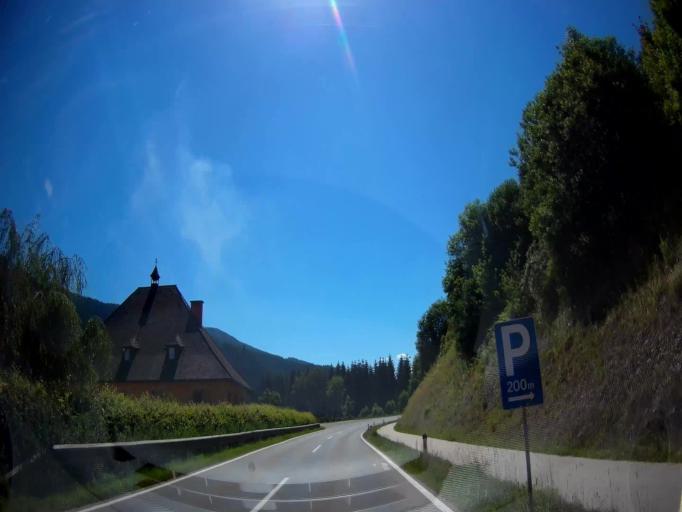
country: AT
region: Carinthia
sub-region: Politischer Bezirk Sankt Veit an der Glan
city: Gurk
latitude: 46.8682
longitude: 14.2684
